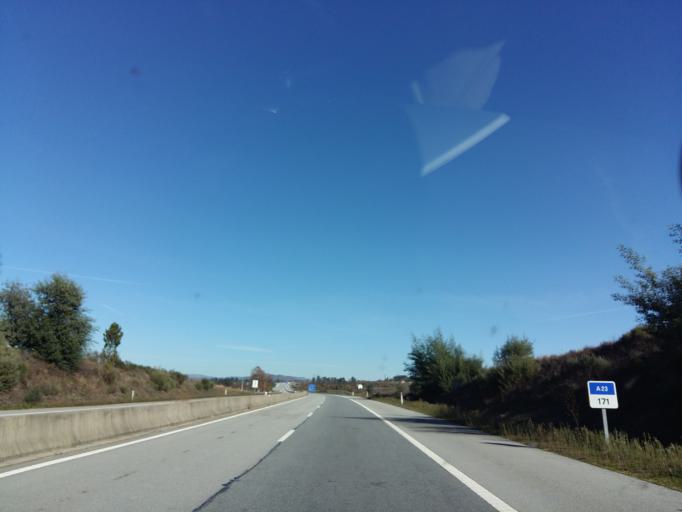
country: PT
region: Castelo Branco
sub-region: Covilha
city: Covilha
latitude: 40.2509
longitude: -7.4524
